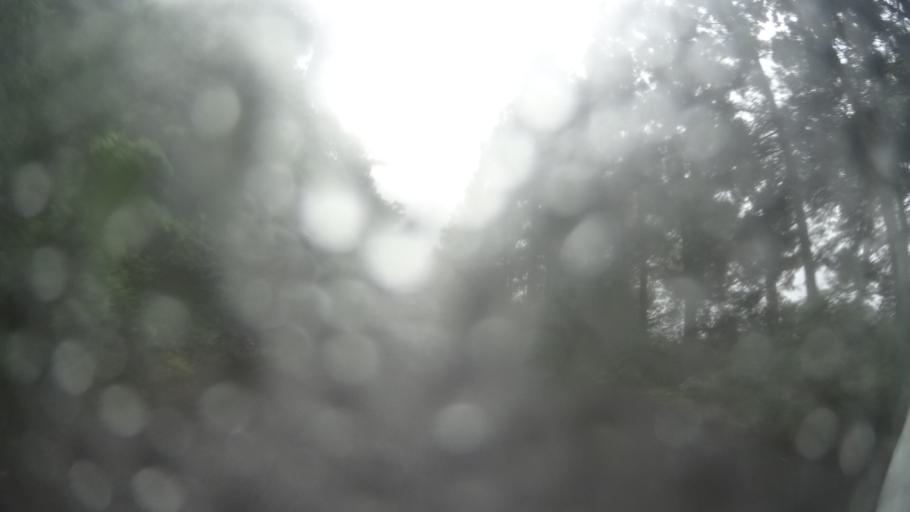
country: JP
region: Kagoshima
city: Nishinoomote
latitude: 30.3041
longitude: 130.5497
